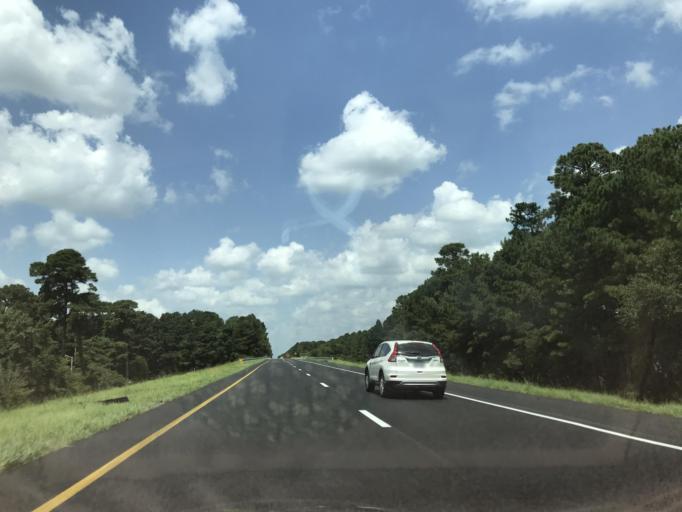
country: US
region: North Carolina
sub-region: Duplin County
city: Warsaw
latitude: 34.9917
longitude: -78.1321
